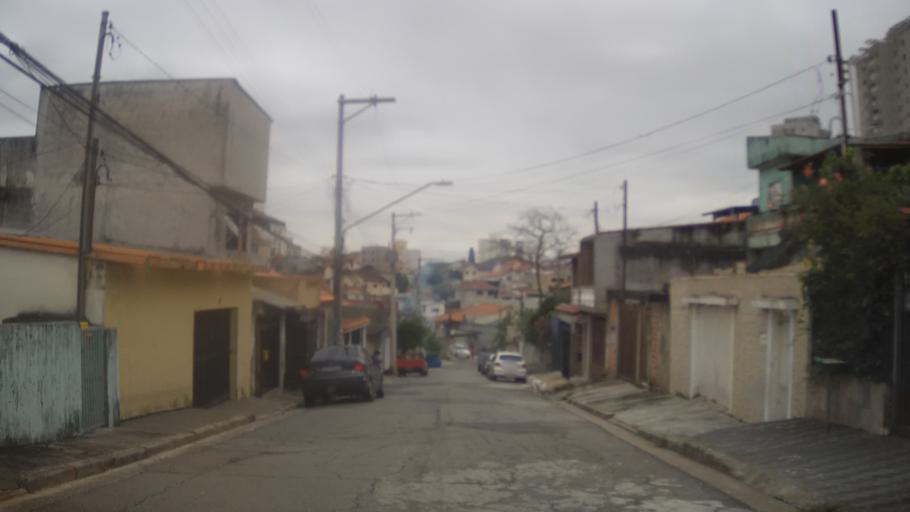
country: BR
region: Sao Paulo
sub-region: Guarulhos
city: Guarulhos
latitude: -23.4506
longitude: -46.5459
